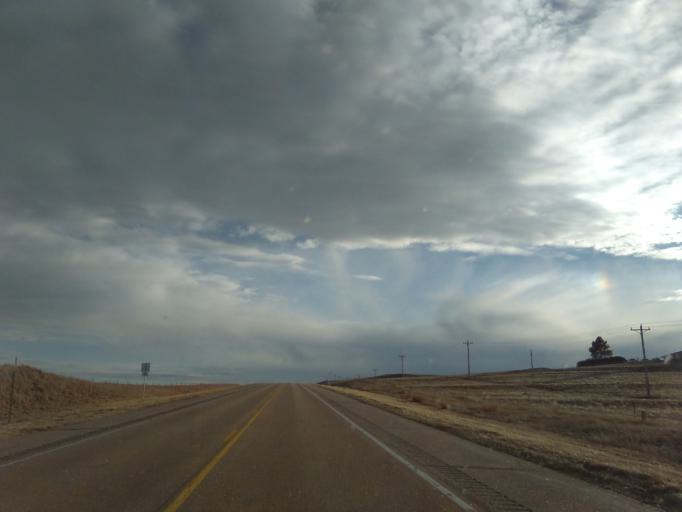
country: US
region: Nebraska
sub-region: Morrill County
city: Bridgeport
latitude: 41.4897
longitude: -102.9839
